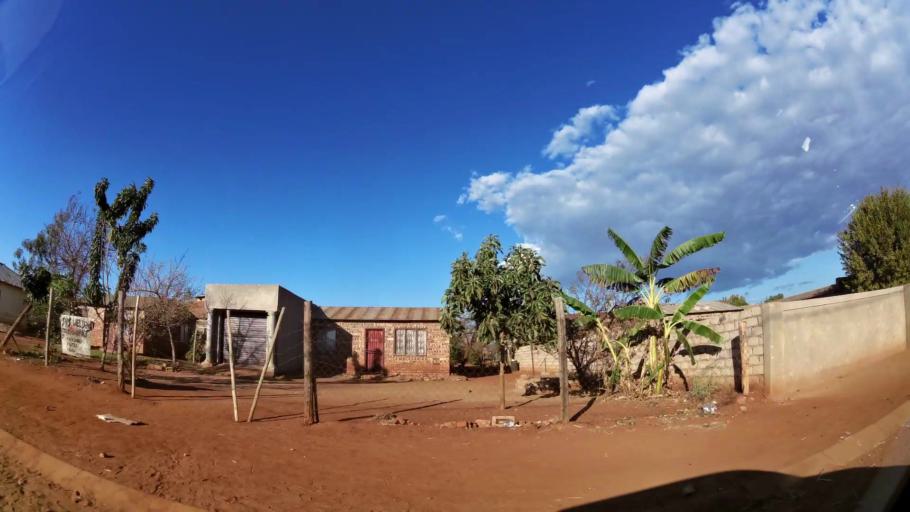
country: ZA
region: Limpopo
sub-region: Waterberg District Municipality
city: Mokopane
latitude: -24.1793
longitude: 28.9802
